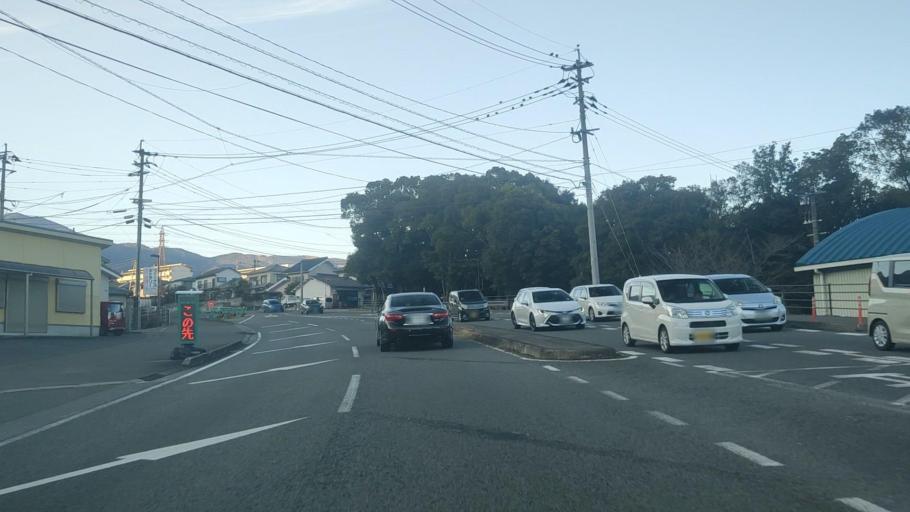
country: JP
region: Oita
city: Beppu
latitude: 33.2884
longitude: 131.4726
